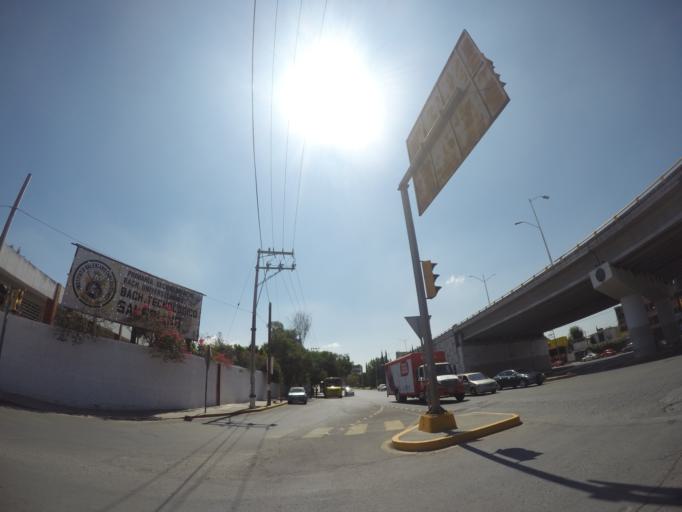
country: MX
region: San Luis Potosi
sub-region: San Luis Potosi
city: San Luis Potosi
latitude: 22.1418
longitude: -101.0137
